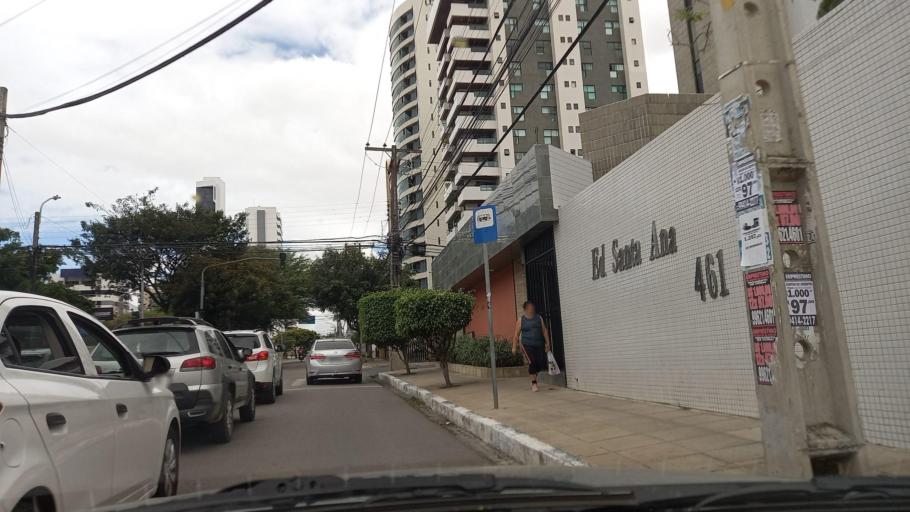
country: BR
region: Pernambuco
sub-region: Caruaru
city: Caruaru
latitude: -8.2700
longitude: -35.9712
